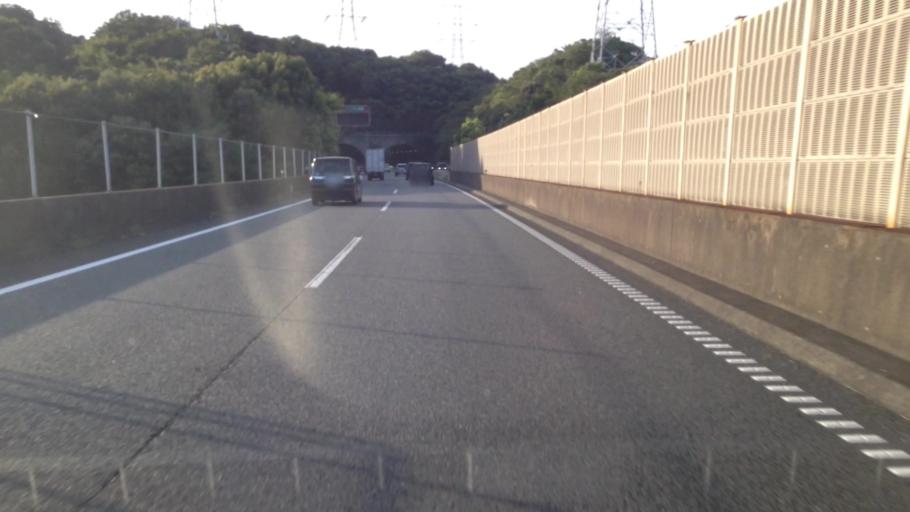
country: JP
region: Kanagawa
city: Zushi
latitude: 35.3207
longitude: 139.6043
